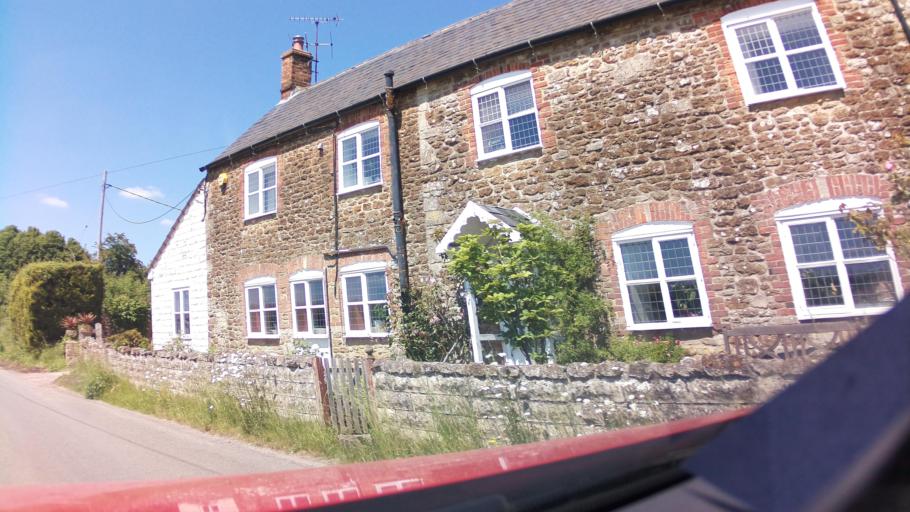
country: GB
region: England
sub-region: Wiltshire
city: Bremhill
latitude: 51.4509
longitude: -2.0637
